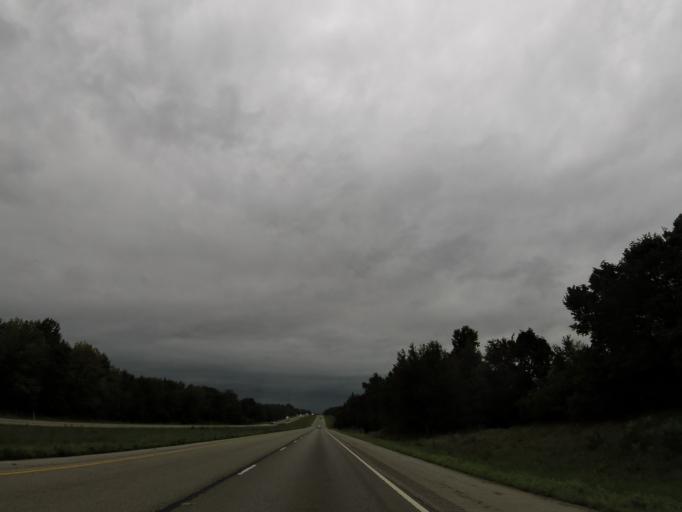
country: US
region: Illinois
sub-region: Massac County
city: Metropolis
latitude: 37.2243
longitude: -88.7049
